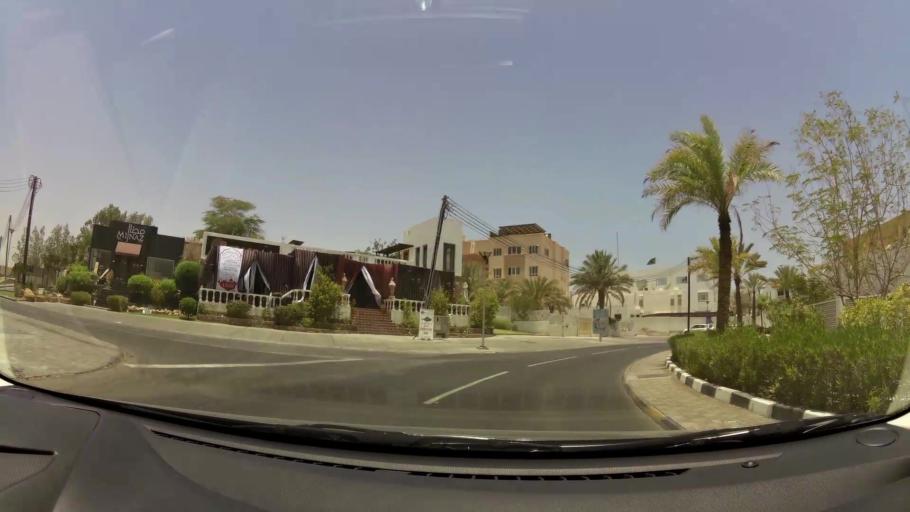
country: OM
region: Muhafazat Masqat
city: Bawshar
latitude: 23.5993
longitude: 58.4543
